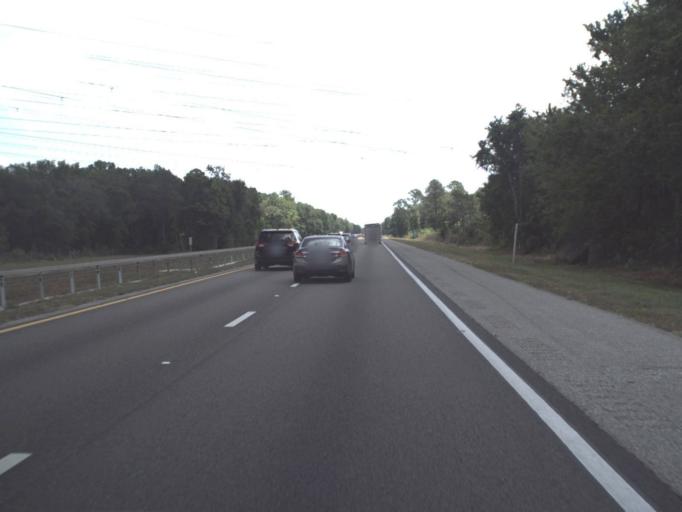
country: US
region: Florida
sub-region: Orange County
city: Wedgefield
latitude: 28.4523
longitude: -81.0125
